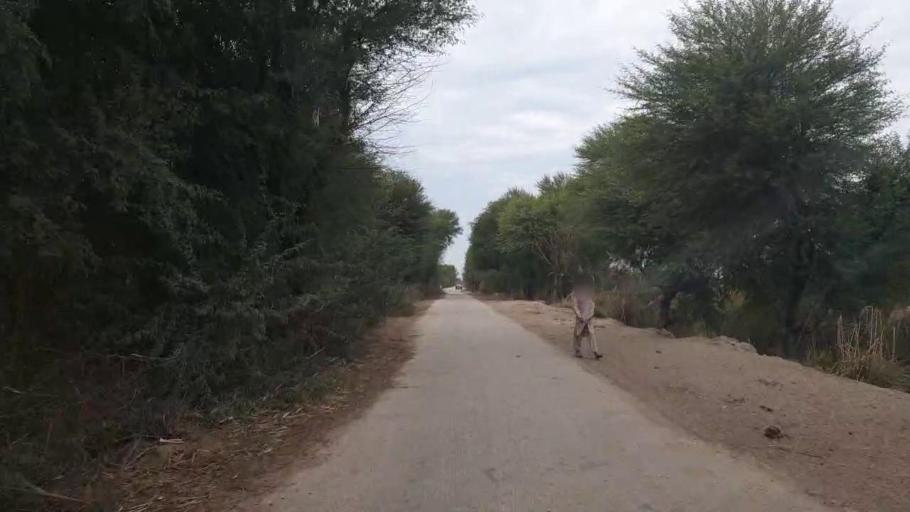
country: PK
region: Sindh
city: Jhol
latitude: 25.9949
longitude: 68.8914
